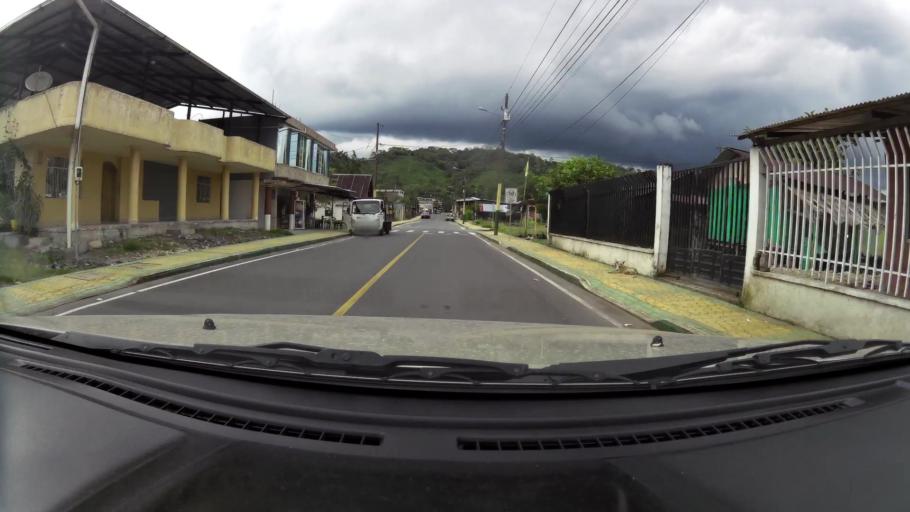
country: EC
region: Pastaza
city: Puyo
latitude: -1.5005
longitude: -78.0193
